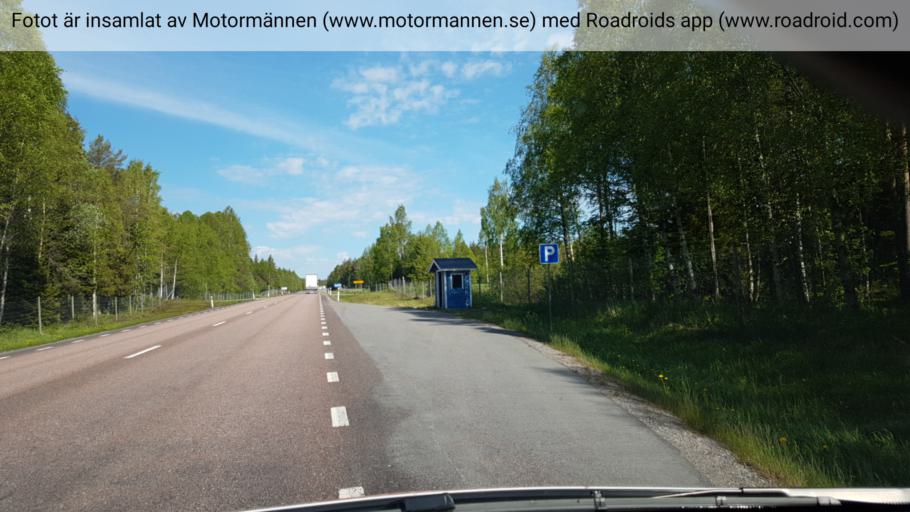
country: SE
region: Vaesterbotten
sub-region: Skelleftea Kommun
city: Burea
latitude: 64.4108
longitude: 21.2950
